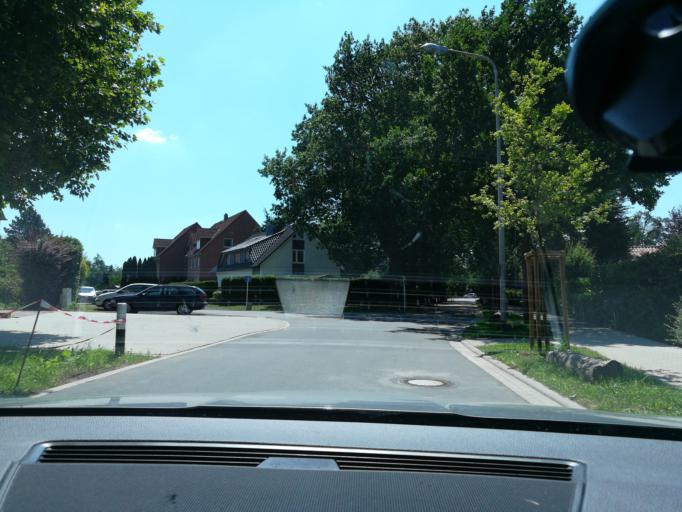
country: DE
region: North Rhine-Westphalia
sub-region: Regierungsbezirk Detmold
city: Minden
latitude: 52.3036
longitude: 8.9078
